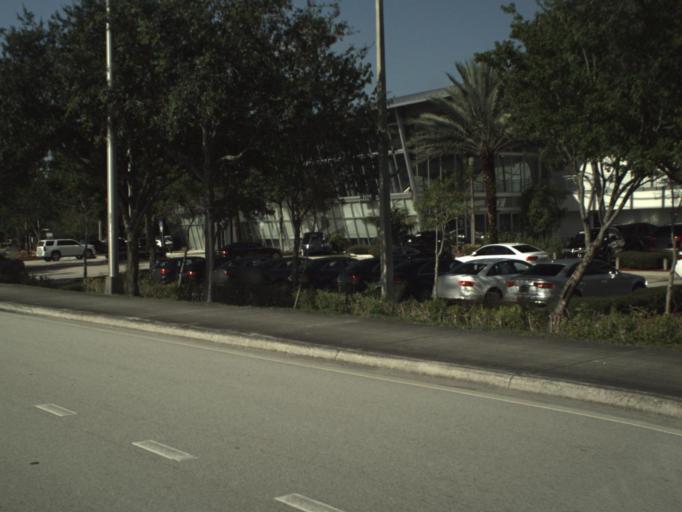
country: US
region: Florida
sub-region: Broward County
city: Parkland
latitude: 26.2980
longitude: -80.2025
